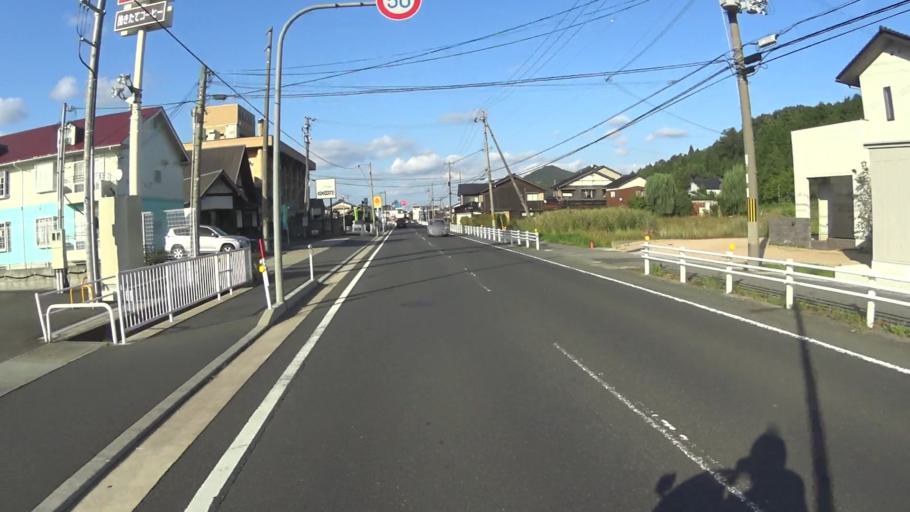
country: JP
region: Hyogo
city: Toyooka
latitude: 35.5876
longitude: 134.8685
